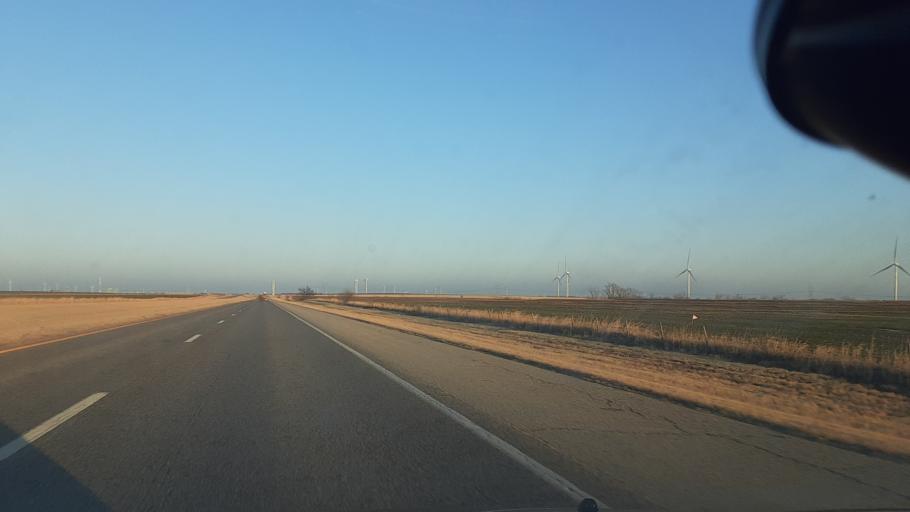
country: US
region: Oklahoma
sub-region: Noble County
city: Perry
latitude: 36.3975
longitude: -97.4965
